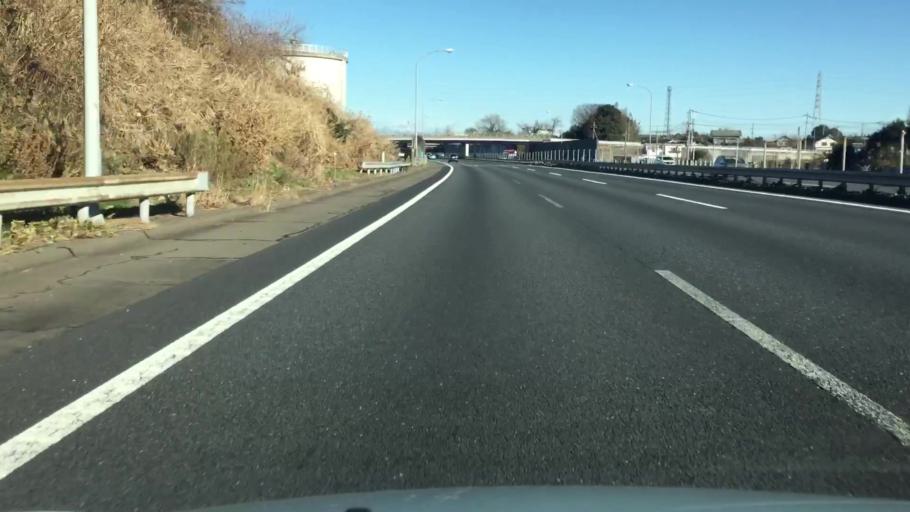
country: JP
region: Saitama
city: Sakado
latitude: 35.9971
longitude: 139.3874
